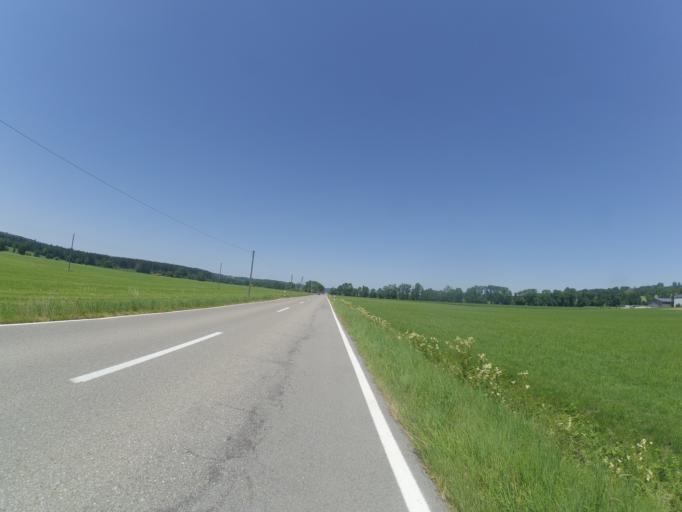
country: DE
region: Bavaria
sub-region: Swabia
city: Bohen
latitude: 47.8931
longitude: 10.3236
